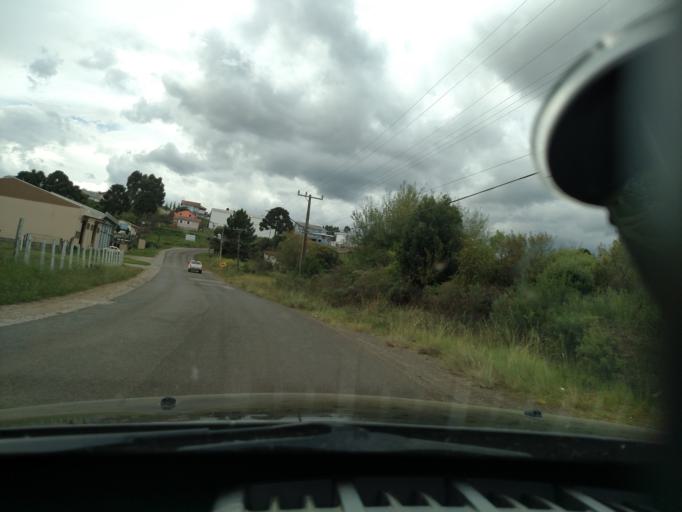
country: BR
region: Santa Catarina
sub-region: Sao Joaquim
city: Sao Joaquim
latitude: -28.2805
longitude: -49.9297
